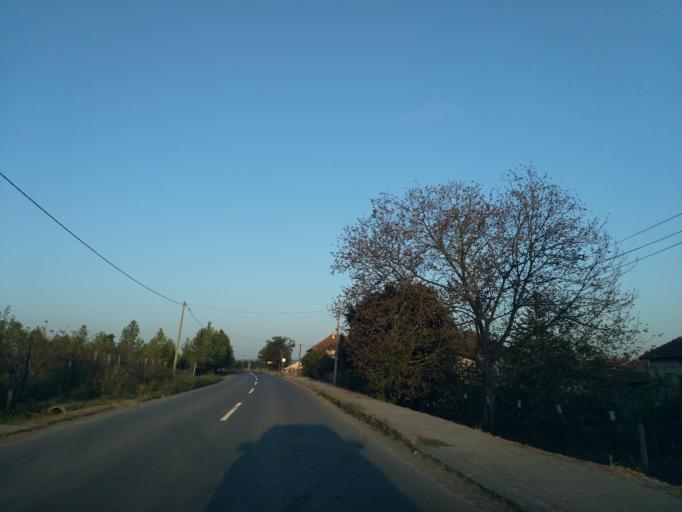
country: RS
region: Central Serbia
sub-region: Rasinski Okrug
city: Trstenik
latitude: 43.6302
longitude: 21.0884
